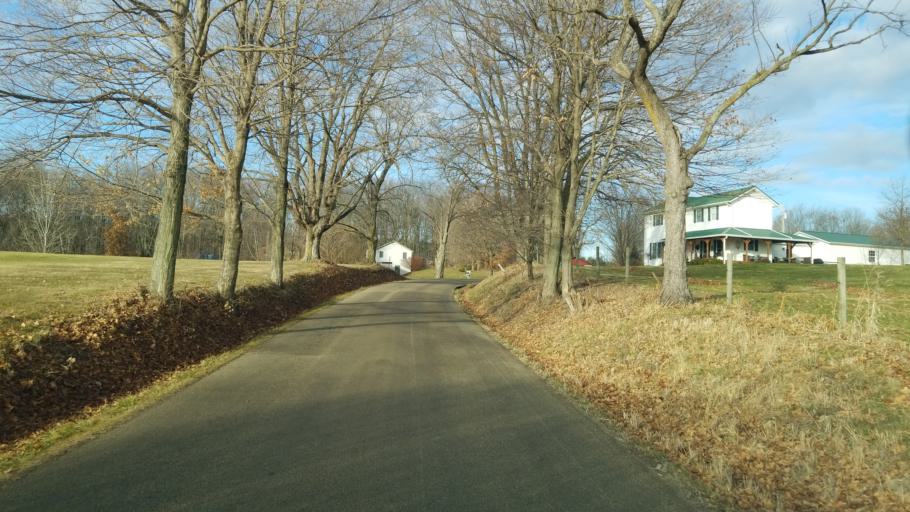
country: US
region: Ohio
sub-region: Knox County
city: Gambier
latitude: 40.3166
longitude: -82.3647
